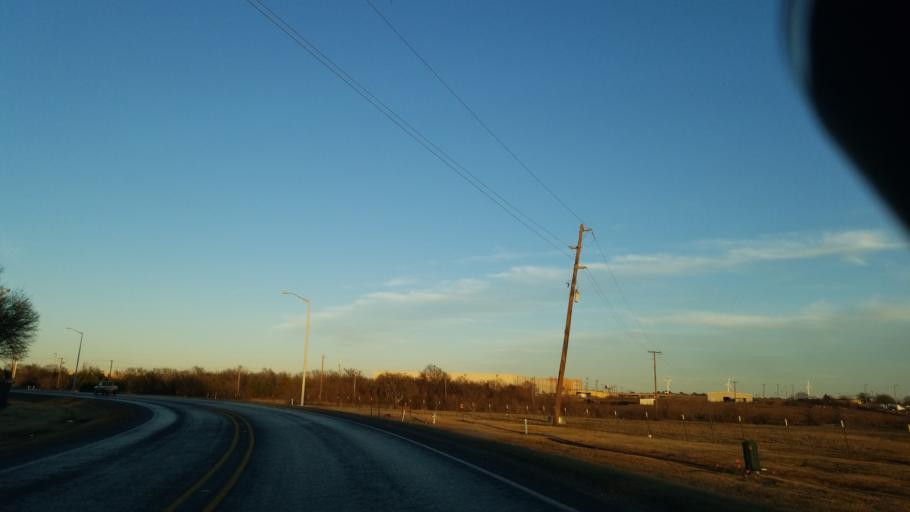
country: US
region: Texas
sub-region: Denton County
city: Denton
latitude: 33.2018
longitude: -97.1749
